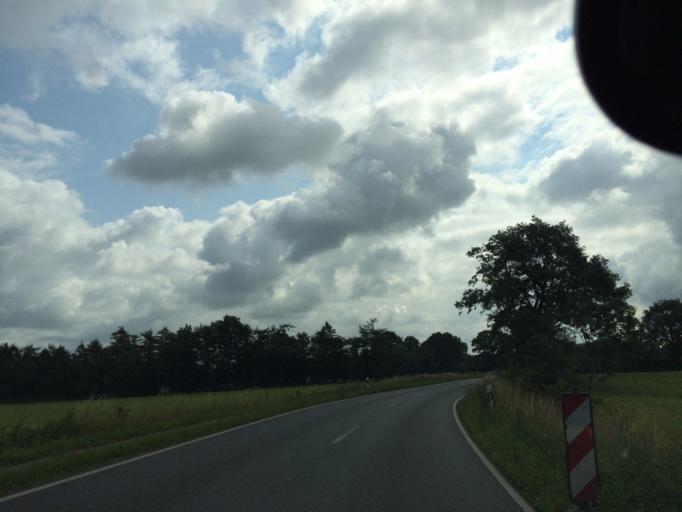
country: DE
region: Schleswig-Holstein
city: Neudorf-Bornstein
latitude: 54.3993
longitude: 9.9451
